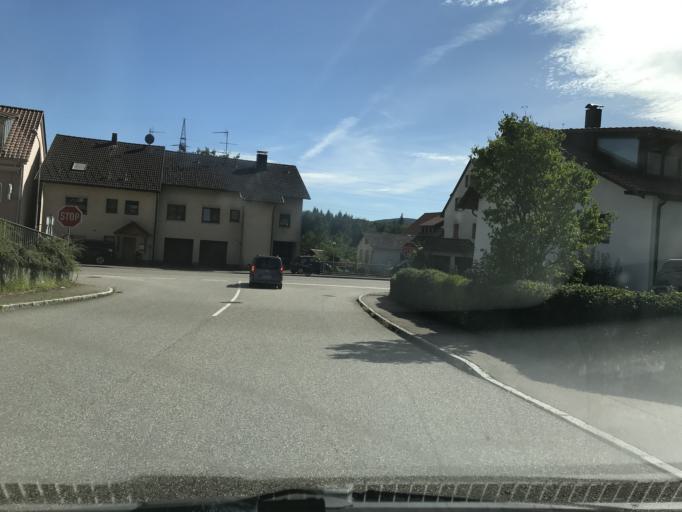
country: DE
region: Baden-Wuerttemberg
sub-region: Freiburg Region
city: Schworstadt
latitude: 47.5912
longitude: 7.8663
